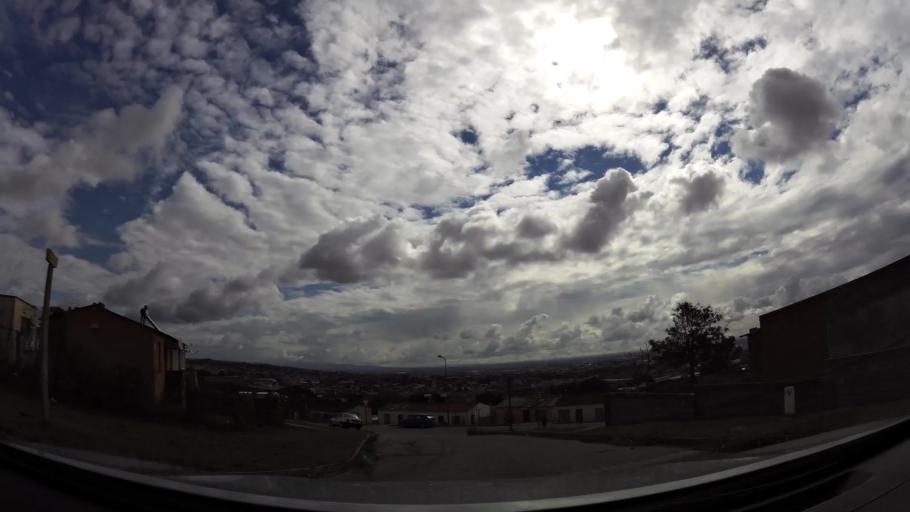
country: ZA
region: Eastern Cape
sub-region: Nelson Mandela Bay Metropolitan Municipality
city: Port Elizabeth
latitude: -33.9321
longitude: 25.5654
